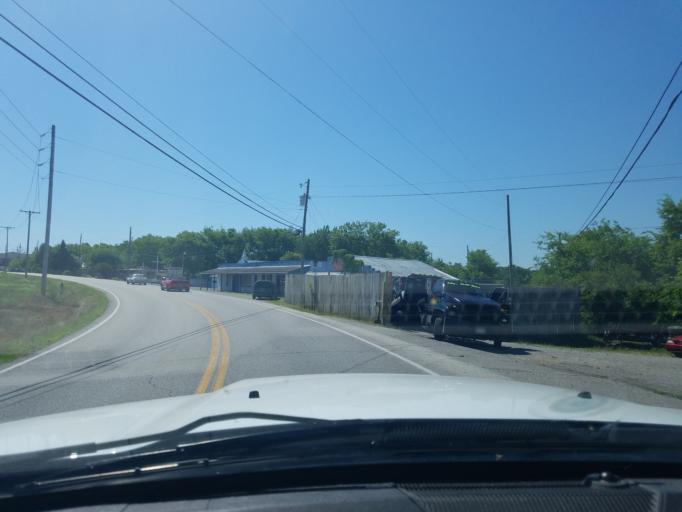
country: US
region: Tennessee
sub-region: Wilson County
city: Lebanon
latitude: 36.1969
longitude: -86.2904
